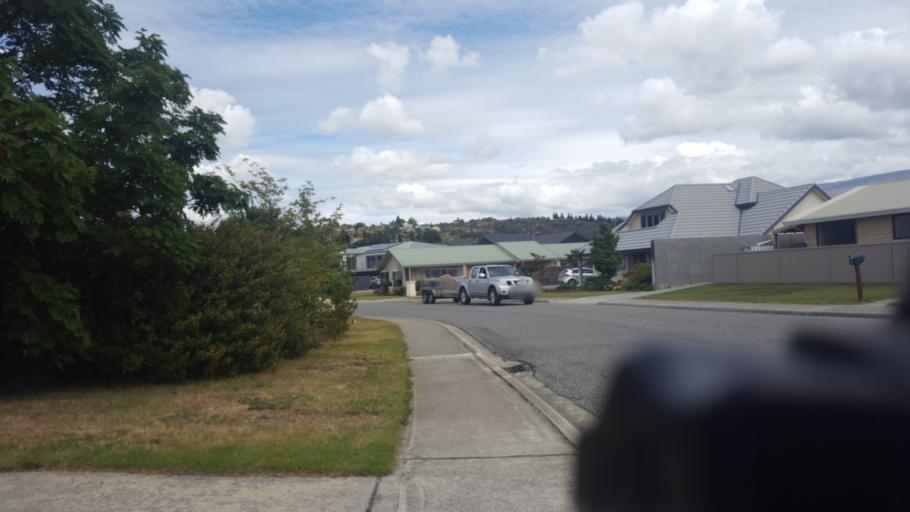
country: NZ
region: Otago
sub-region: Queenstown-Lakes District
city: Wanaka
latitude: -45.2516
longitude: 169.3833
